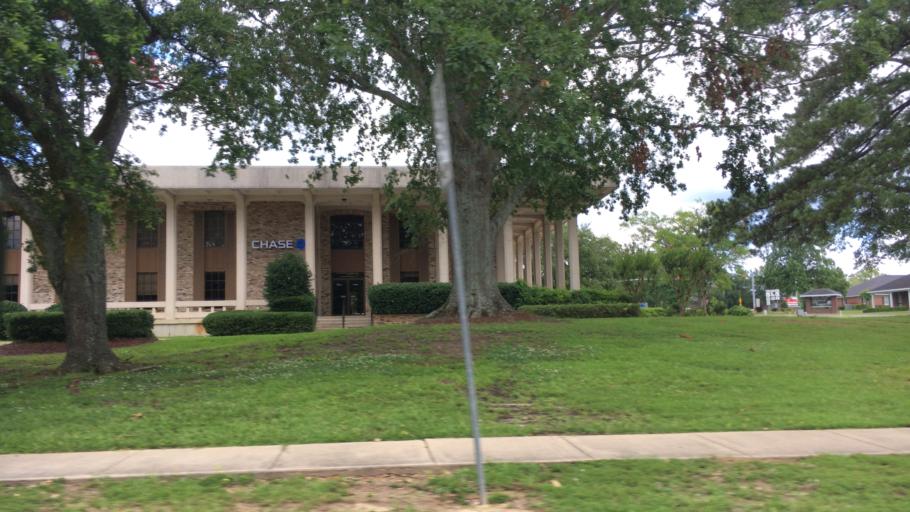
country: US
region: Louisiana
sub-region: Lincoln Parish
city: Ruston
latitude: 32.5319
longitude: -92.6391
